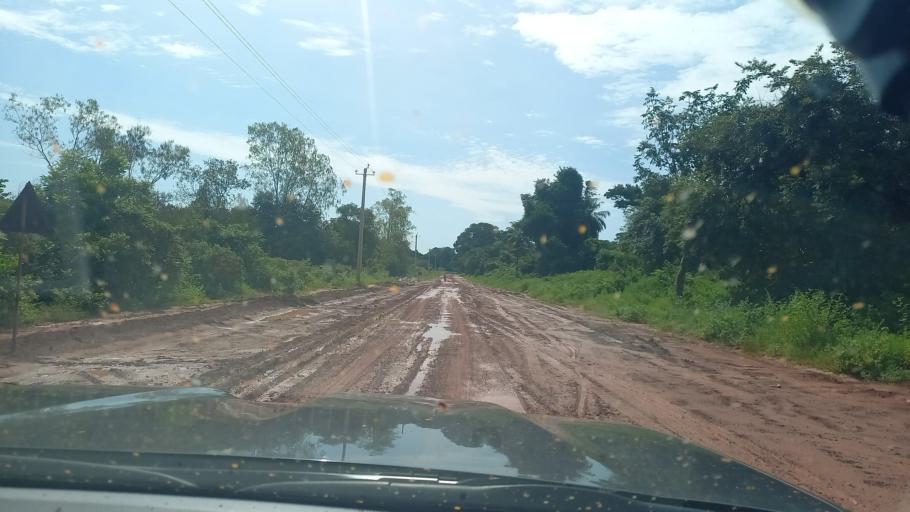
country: SN
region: Ziguinchor
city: Ziguinchor
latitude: 12.6699
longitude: -16.1879
